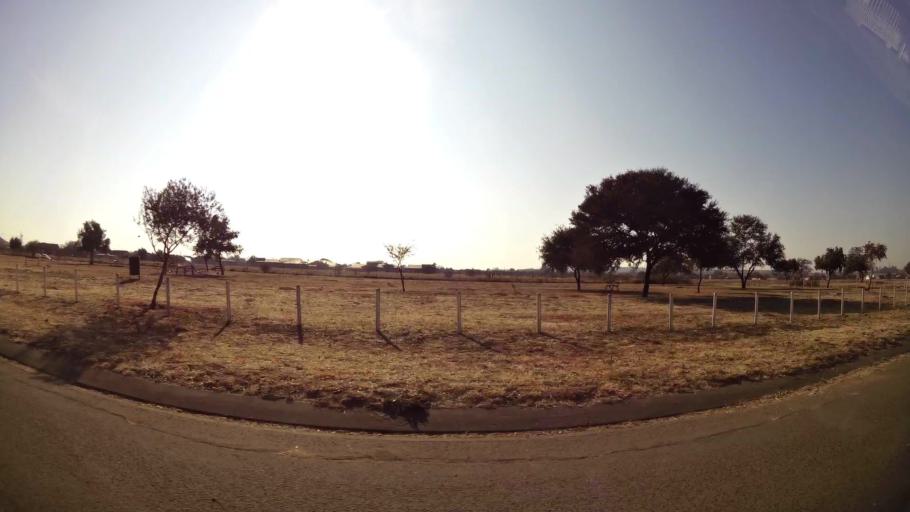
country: ZA
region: Orange Free State
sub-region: Mangaung Metropolitan Municipality
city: Bloemfontein
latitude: -29.1821
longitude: 26.1753
